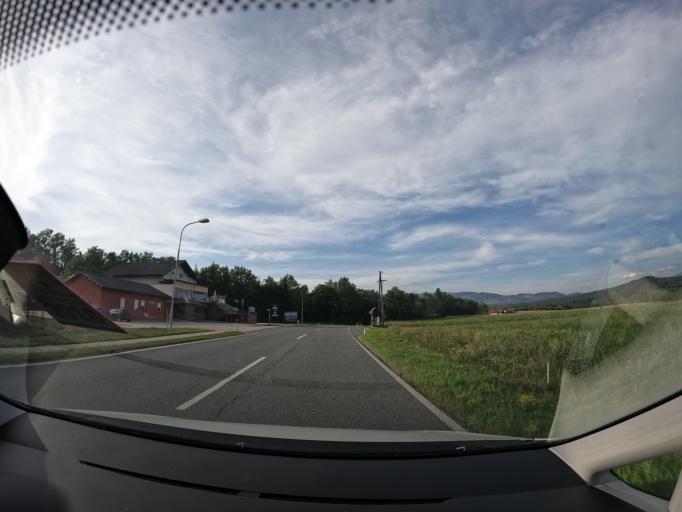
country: AT
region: Carinthia
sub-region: Politischer Bezirk Volkermarkt
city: Voelkermarkt
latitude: 46.6380
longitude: 14.6295
